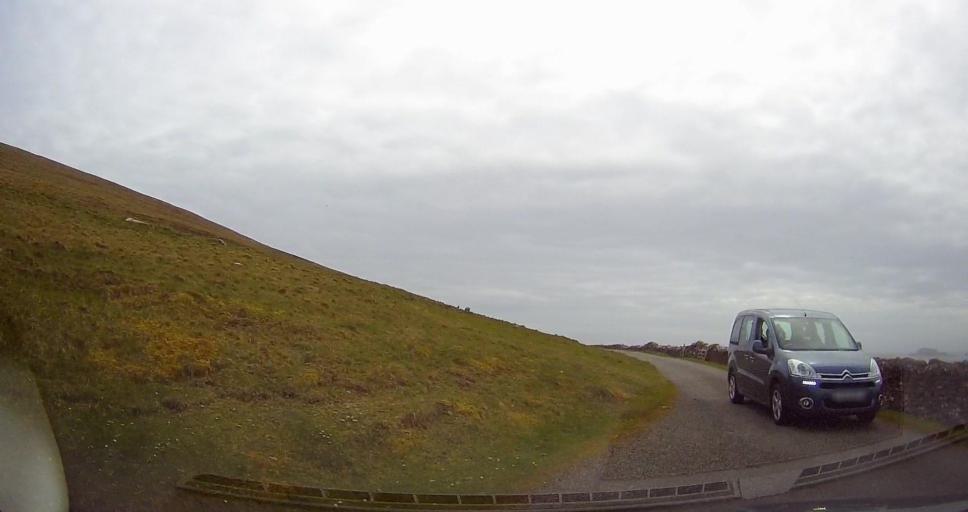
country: GB
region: Scotland
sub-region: Shetland Islands
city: Sandwick
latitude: 59.8699
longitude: -1.2787
